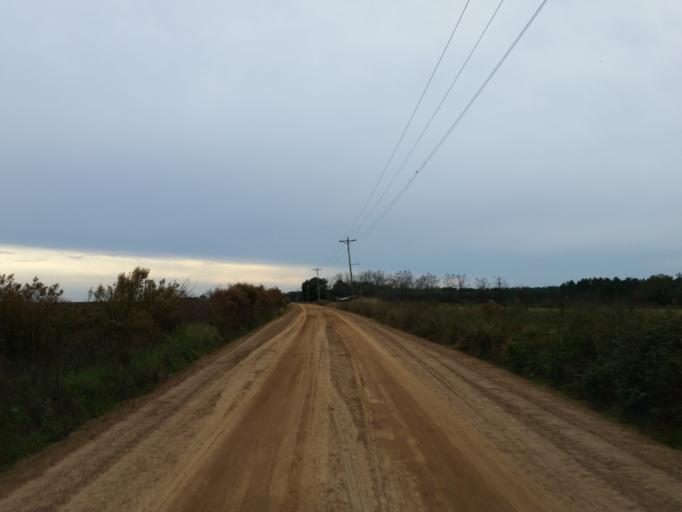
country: US
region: Georgia
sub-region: Crisp County
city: Cordele
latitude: 31.9001
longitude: -83.7137
